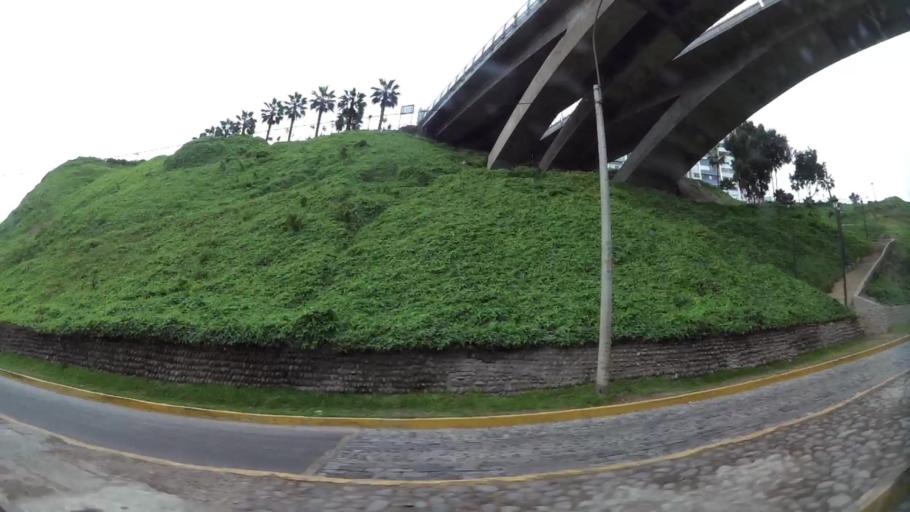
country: PE
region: Lima
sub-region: Lima
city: San Isidro
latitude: -12.1276
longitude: -77.0359
